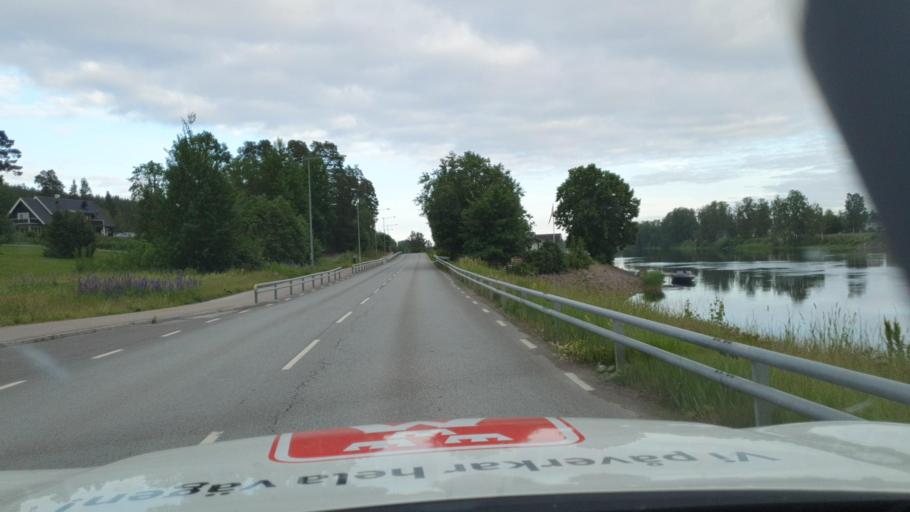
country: SE
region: Vaermland
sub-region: Karlstads Kommun
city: Karlstad
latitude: 59.4208
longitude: 13.4845
